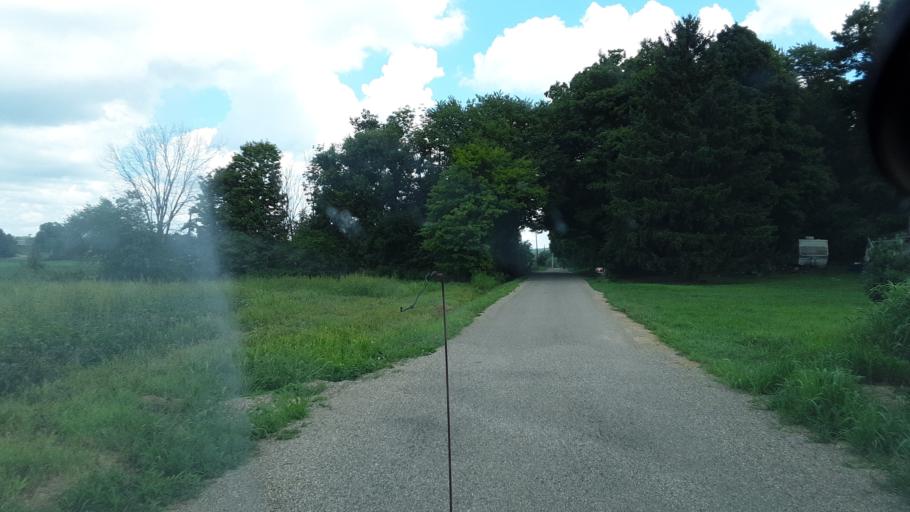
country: US
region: Ohio
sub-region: Licking County
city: Utica
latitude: 40.2616
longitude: -82.4050
